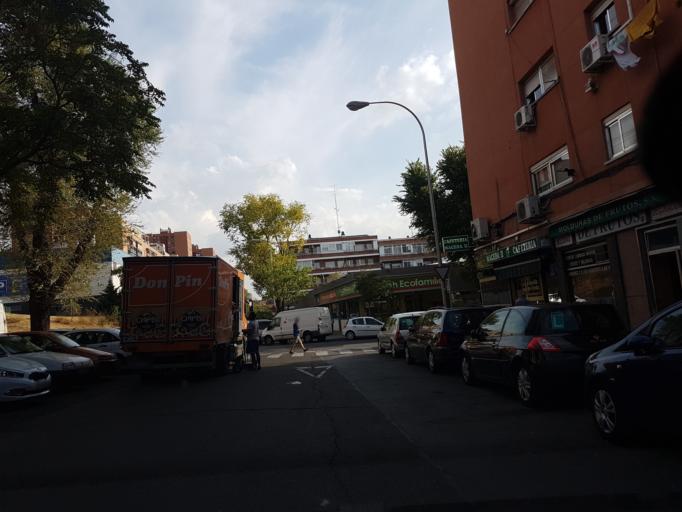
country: ES
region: Madrid
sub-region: Provincia de Madrid
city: Puente de Vallecas
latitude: 40.4036
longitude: -3.6609
